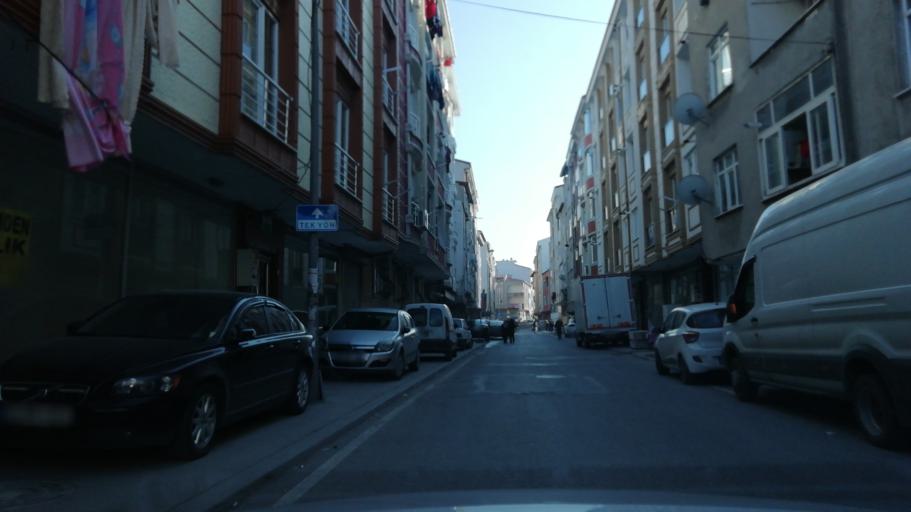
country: TR
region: Istanbul
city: Esenyurt
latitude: 41.0322
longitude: 28.6892
